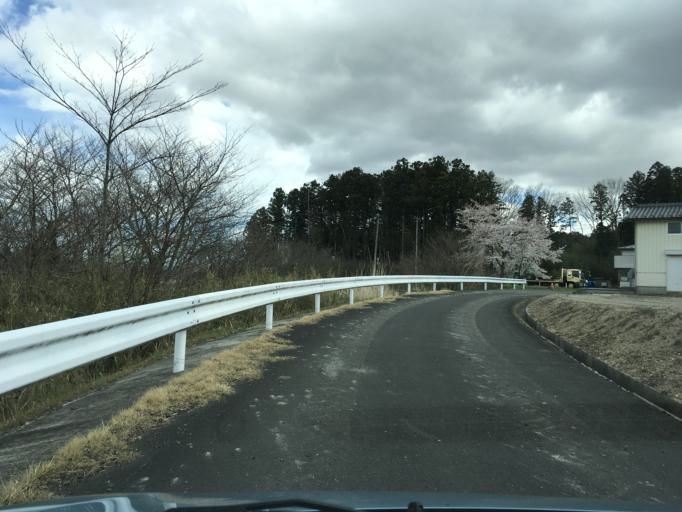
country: JP
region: Miyagi
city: Wakuya
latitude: 38.6803
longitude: 141.1234
